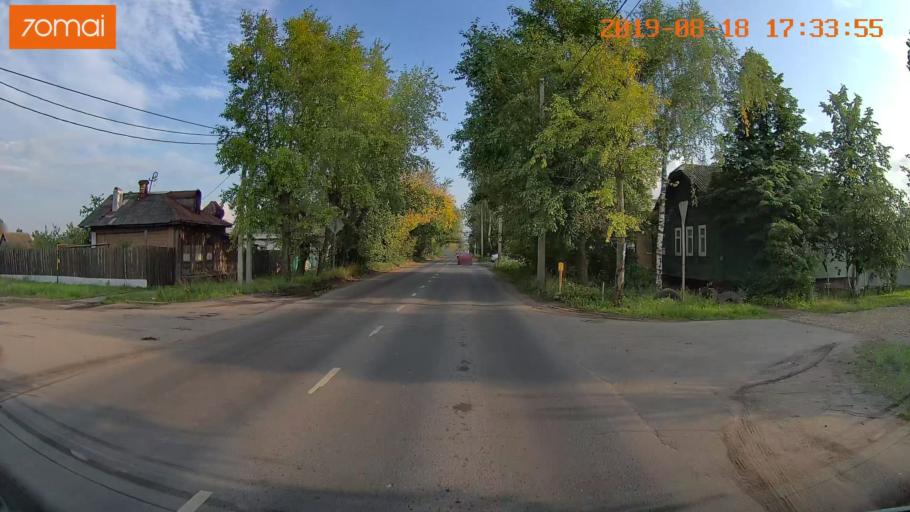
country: RU
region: Ivanovo
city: Bogorodskoye
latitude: 56.9970
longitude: 41.0300
